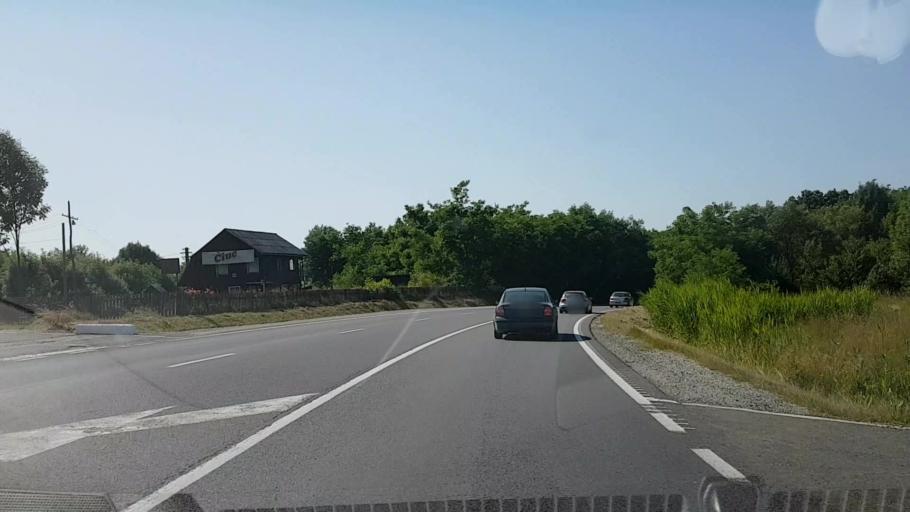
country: RO
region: Sibiu
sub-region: Comuna Carta
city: Carta
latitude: 45.7596
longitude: 24.5396
